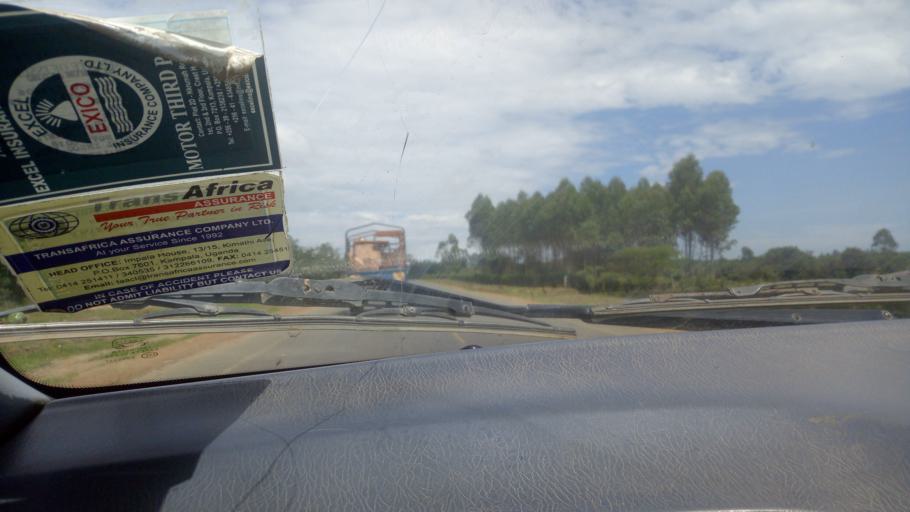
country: UG
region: Western Region
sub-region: Mbarara District
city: Bwizibwera
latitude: -0.4277
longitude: 30.5711
